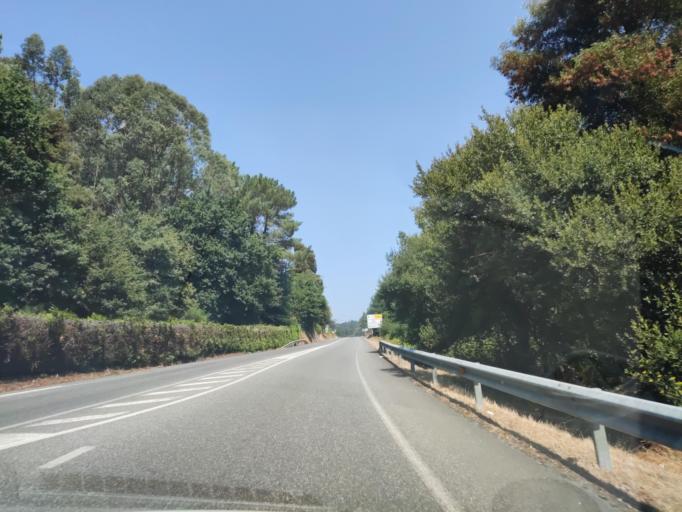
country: ES
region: Galicia
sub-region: Provincia de Pontevedra
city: Redondela
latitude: 42.2406
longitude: -8.5966
